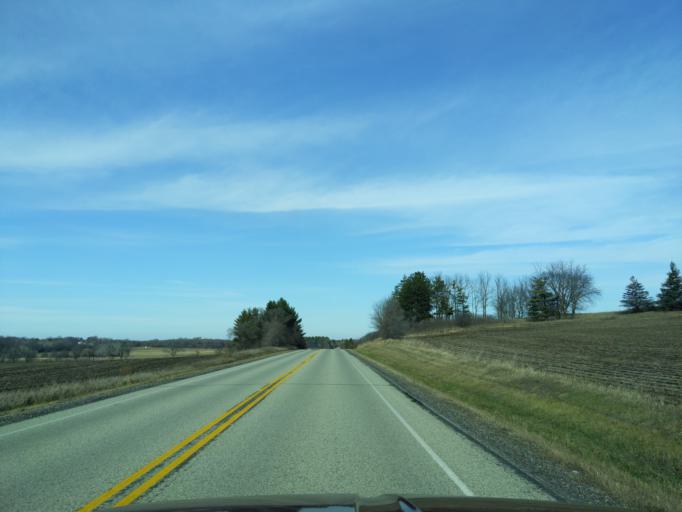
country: US
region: Wisconsin
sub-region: Jefferson County
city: Palmyra
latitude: 42.7889
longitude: -88.6025
